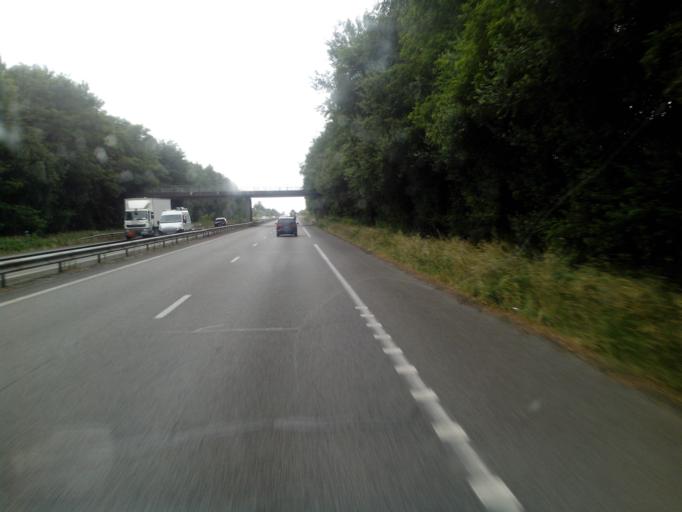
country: FR
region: Pays de la Loire
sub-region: Departement de la Loire-Atlantique
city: Treillieres
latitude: 47.3549
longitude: -1.6563
